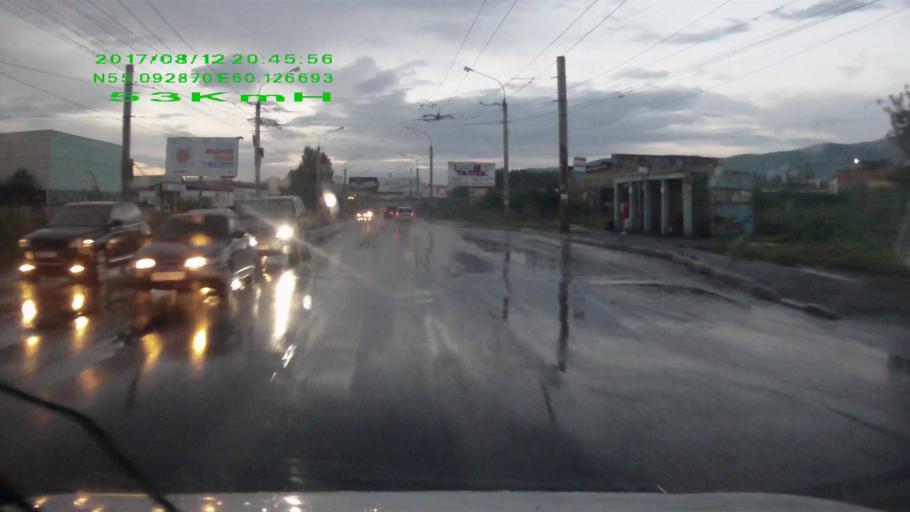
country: RU
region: Chelyabinsk
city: Miass
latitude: 55.0931
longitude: 60.1268
